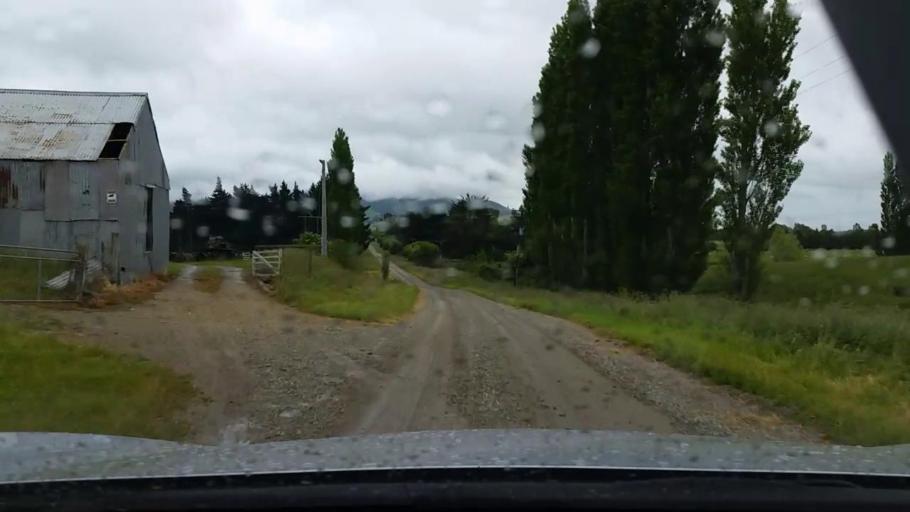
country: NZ
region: Southland
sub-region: Gore District
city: Gore
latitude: -46.0731
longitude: 168.9631
